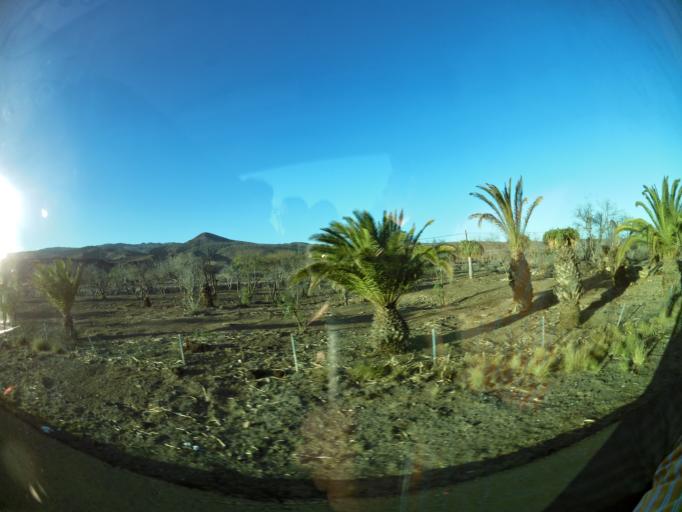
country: ES
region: Canary Islands
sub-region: Provincia de Las Palmas
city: Playa del Ingles
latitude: 27.7847
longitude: -15.5102
